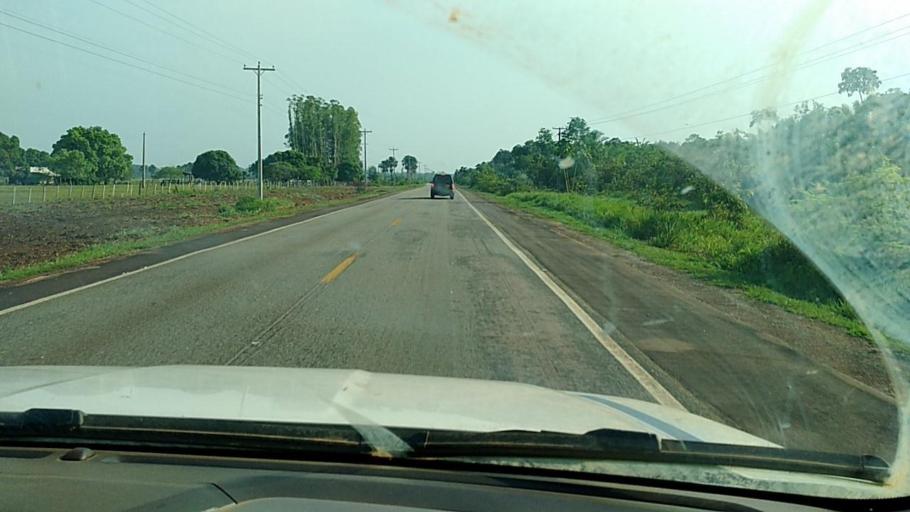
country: BR
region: Rondonia
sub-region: Porto Velho
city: Porto Velho
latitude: -8.2351
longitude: -63.9275
